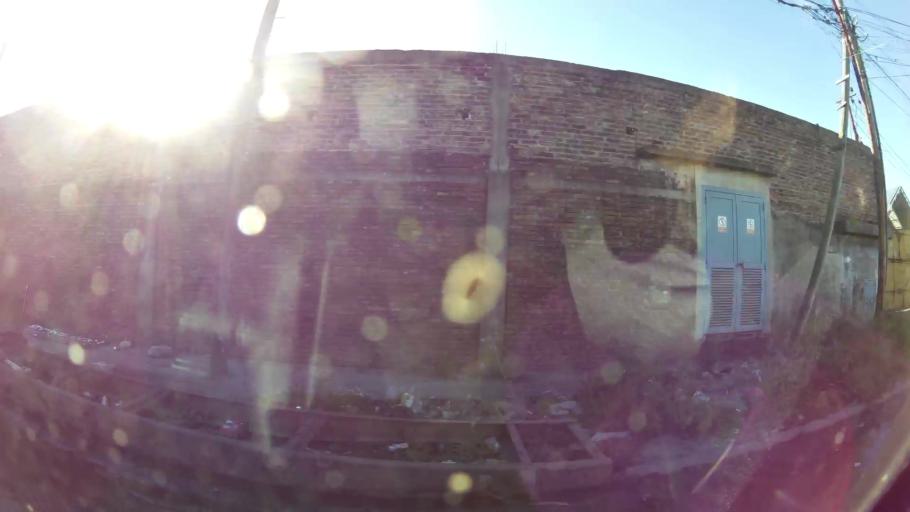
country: AR
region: Buenos Aires
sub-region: Partido de Quilmes
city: Quilmes
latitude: -34.7482
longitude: -58.3130
